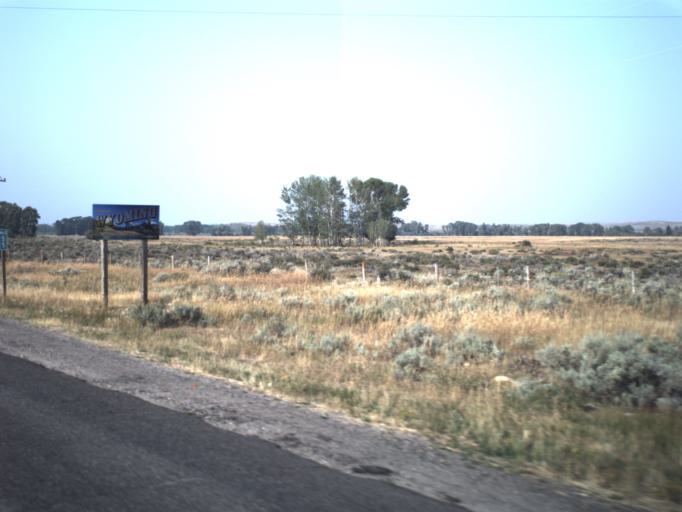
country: US
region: Wyoming
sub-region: Uinta County
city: Evanston
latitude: 40.9969
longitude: -110.8646
